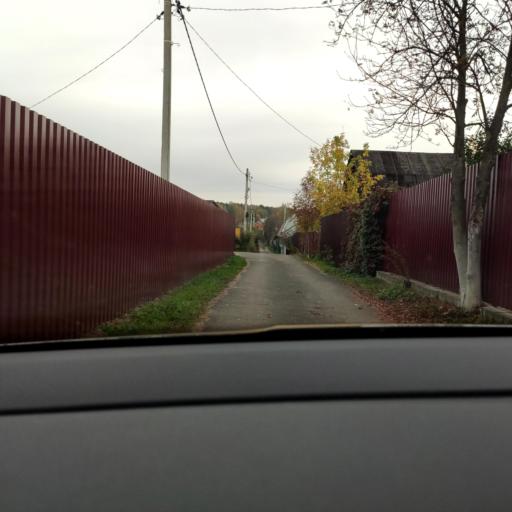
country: RU
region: Moskovskaya
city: Zagoryanskiy
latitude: 55.9641
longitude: 37.9666
